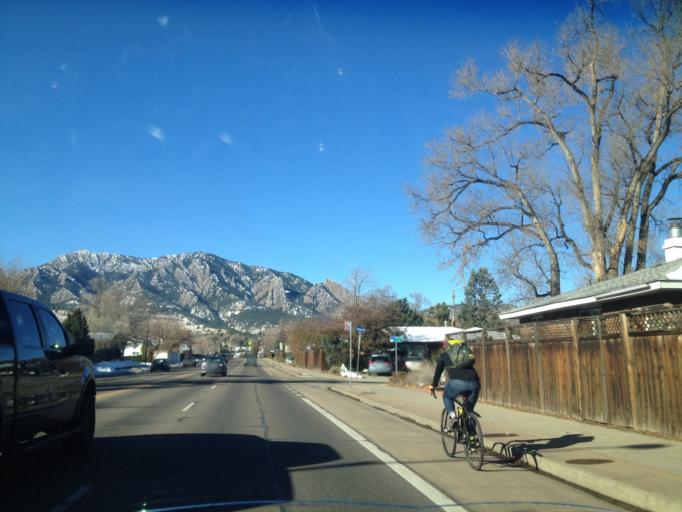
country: US
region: Colorado
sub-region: Boulder County
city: Boulder
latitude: 39.9859
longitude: -105.2449
